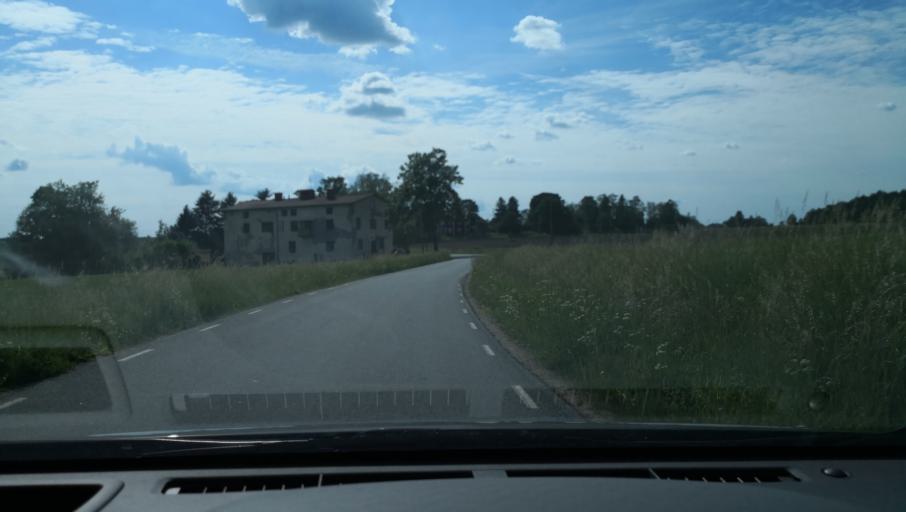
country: SE
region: Uppsala
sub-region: Enkopings Kommun
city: Orsundsbro
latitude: 59.8162
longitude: 17.3491
